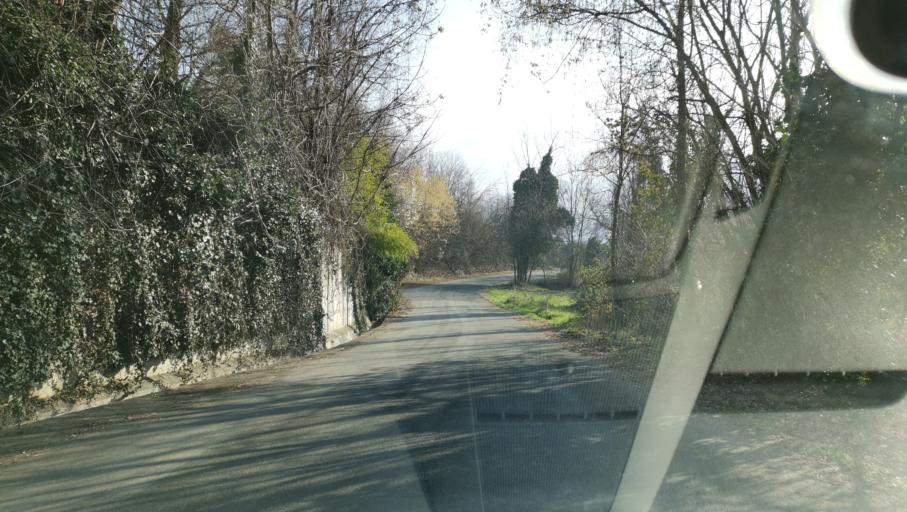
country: IT
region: Piedmont
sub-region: Provincia di Torino
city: Castagneto Po
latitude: 45.1458
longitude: 7.8851
